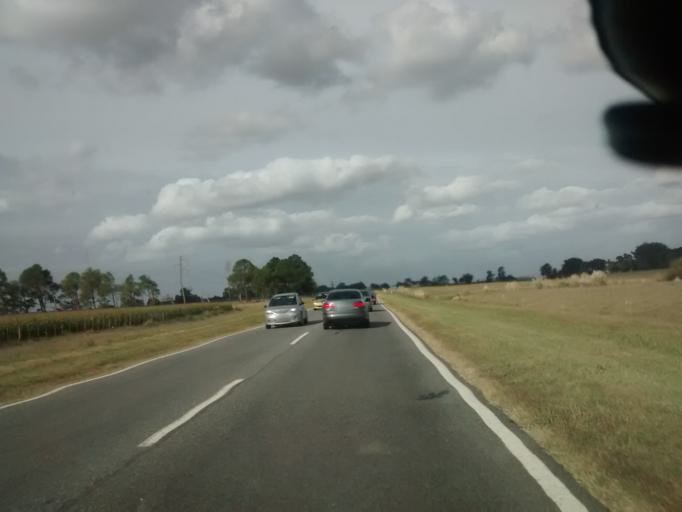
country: AR
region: Buenos Aires
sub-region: Partido de Balcarce
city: Balcarce
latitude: -37.6717
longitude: -58.4719
